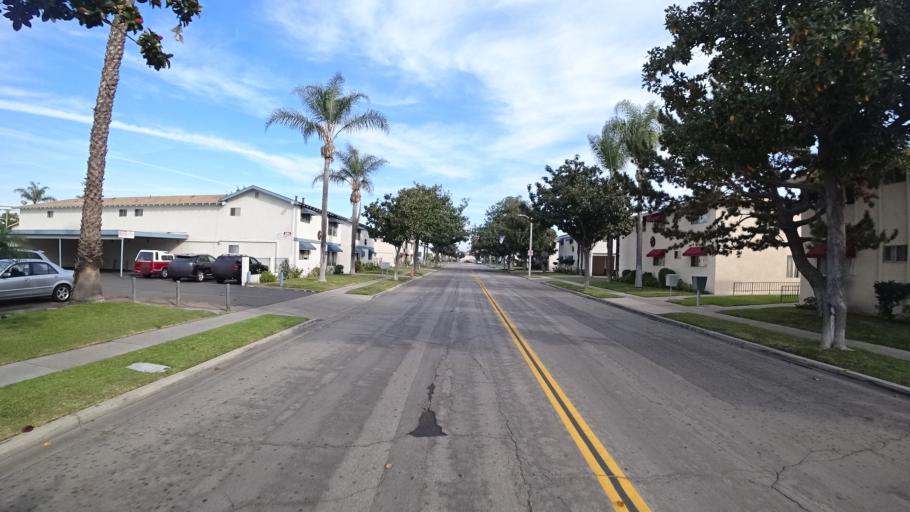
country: US
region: California
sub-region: Orange County
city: Garden Grove
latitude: 33.7576
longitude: -117.9109
